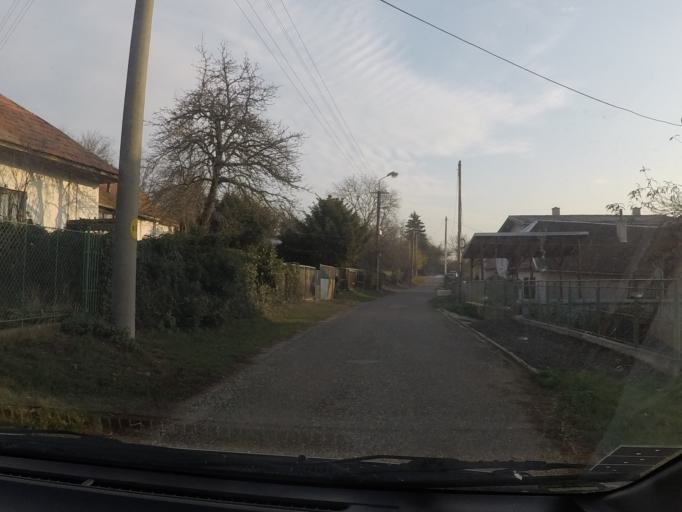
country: SK
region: Nitriansky
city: Svodin
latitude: 48.0351
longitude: 18.4715
